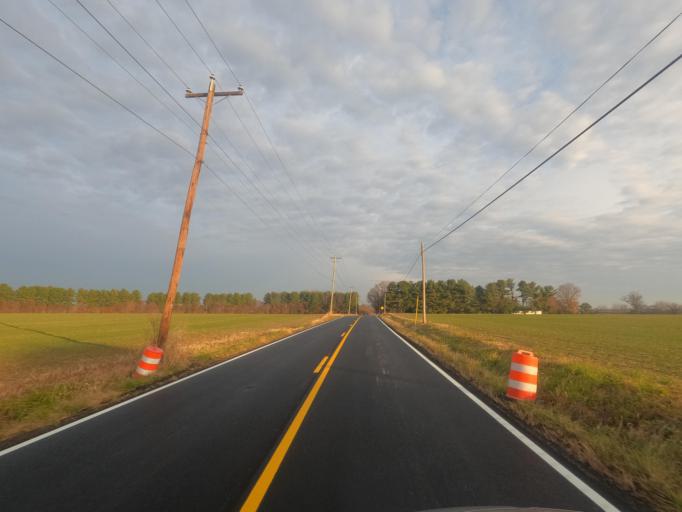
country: US
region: Delaware
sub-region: New Castle County
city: Townsend
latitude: 39.2674
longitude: -75.8379
